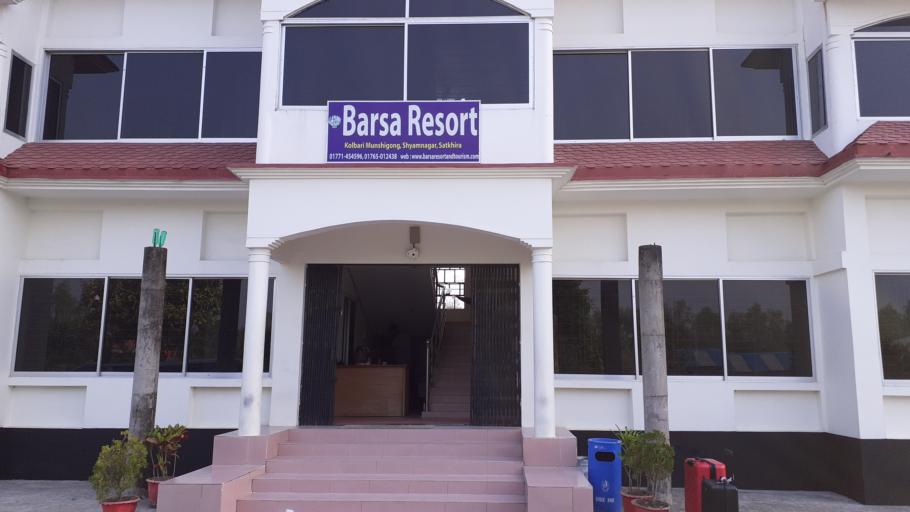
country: IN
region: West Bengal
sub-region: North 24 Parganas
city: Gosaba
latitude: 22.2687
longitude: 89.2043
